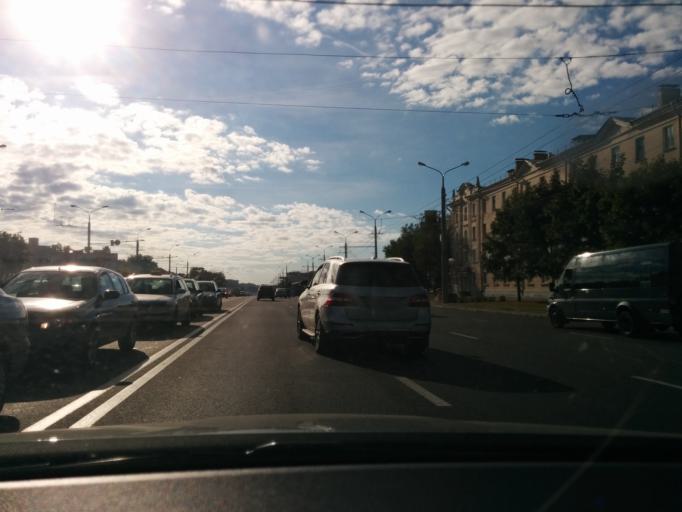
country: BY
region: Minsk
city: Vyaliki Trastsyanets
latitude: 53.8693
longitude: 27.6477
